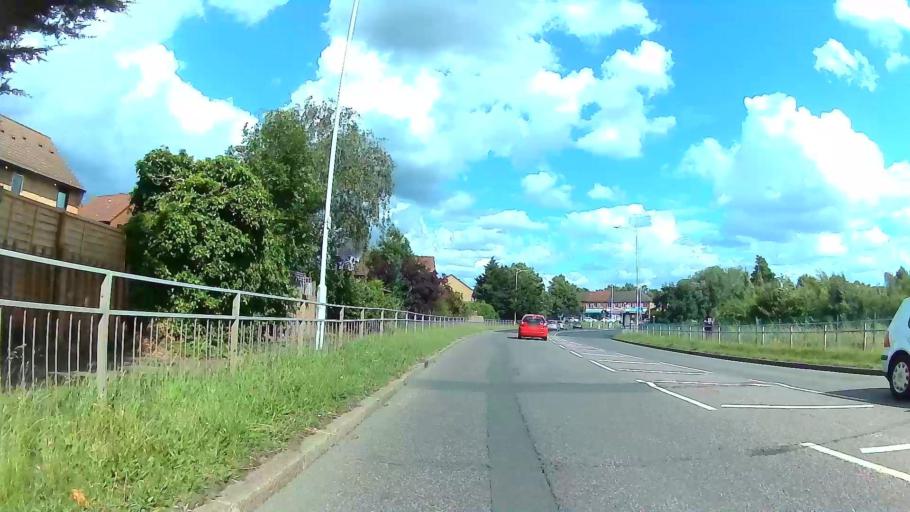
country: GB
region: England
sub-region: Greater London
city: Woodford Green
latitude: 51.6012
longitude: 0.0415
